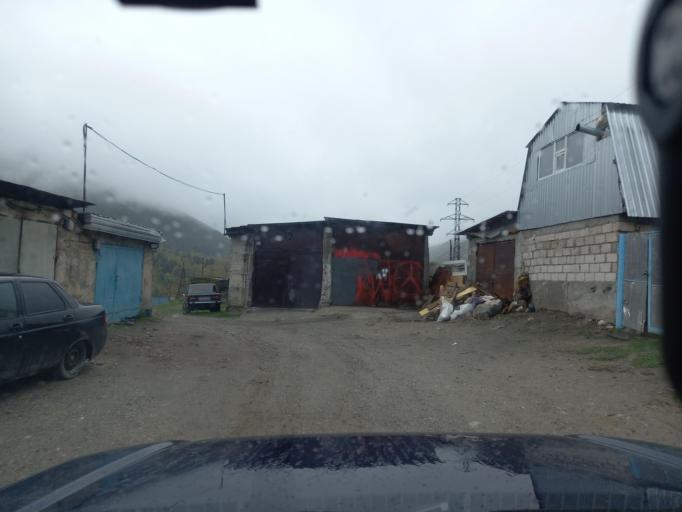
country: RU
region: Kabardino-Balkariya
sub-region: El'brusskiy Rayon
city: El'brus
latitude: 43.2775
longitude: 42.6843
